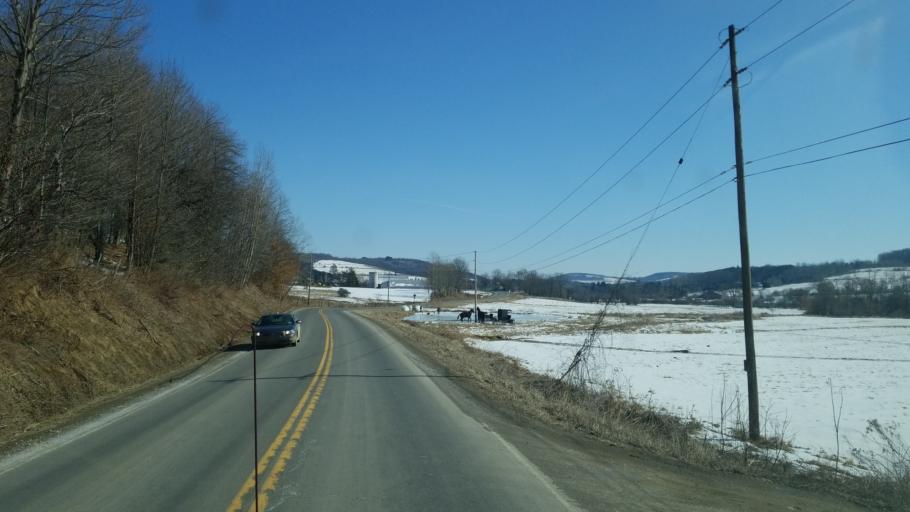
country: US
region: Pennsylvania
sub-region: Tioga County
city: Elkland
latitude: 42.0761
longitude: -77.4244
